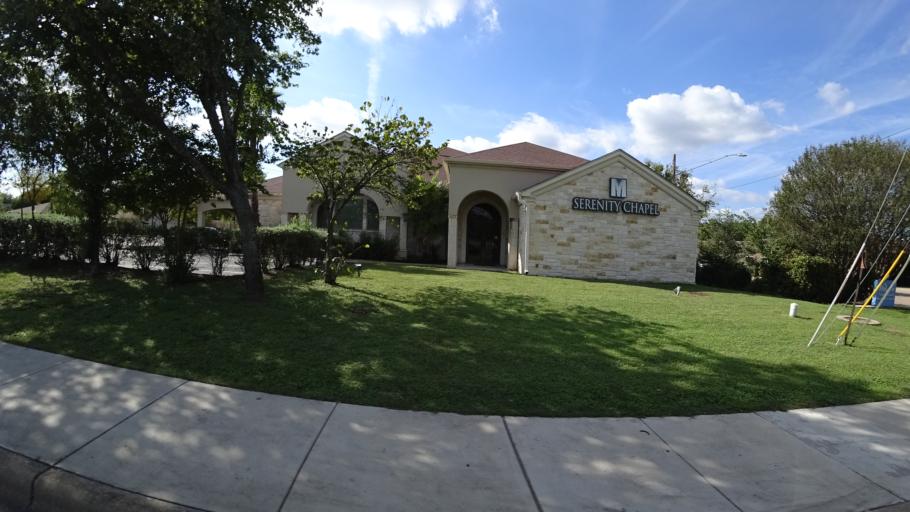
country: US
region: Texas
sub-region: Travis County
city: Onion Creek
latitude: 30.2019
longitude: -97.7848
